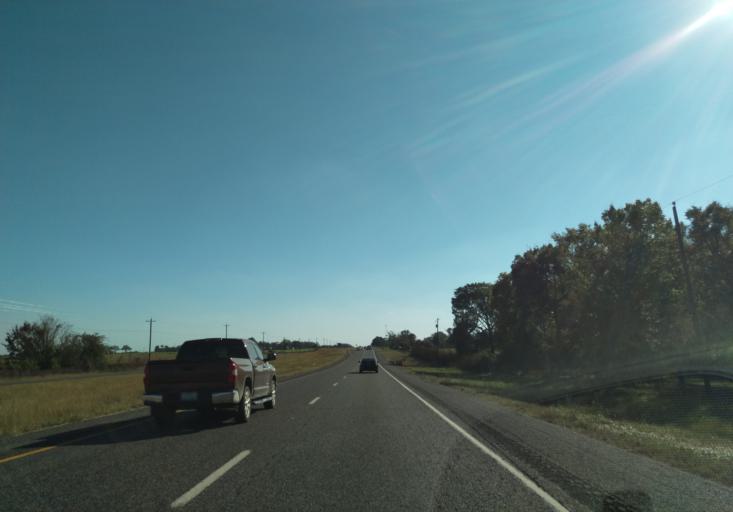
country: US
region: Texas
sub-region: Waller County
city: Hempstead
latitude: 30.1486
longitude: -96.0700
